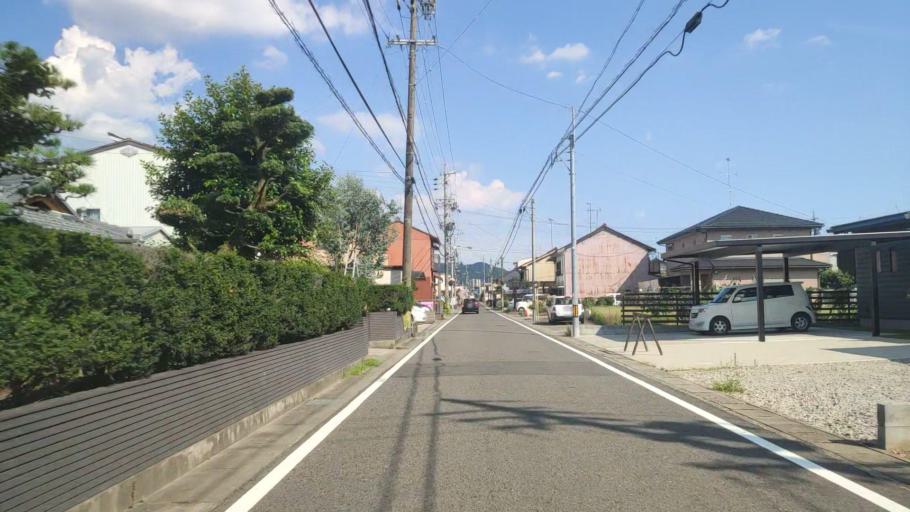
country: JP
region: Gifu
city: Gifu-shi
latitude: 35.4443
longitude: 136.7427
